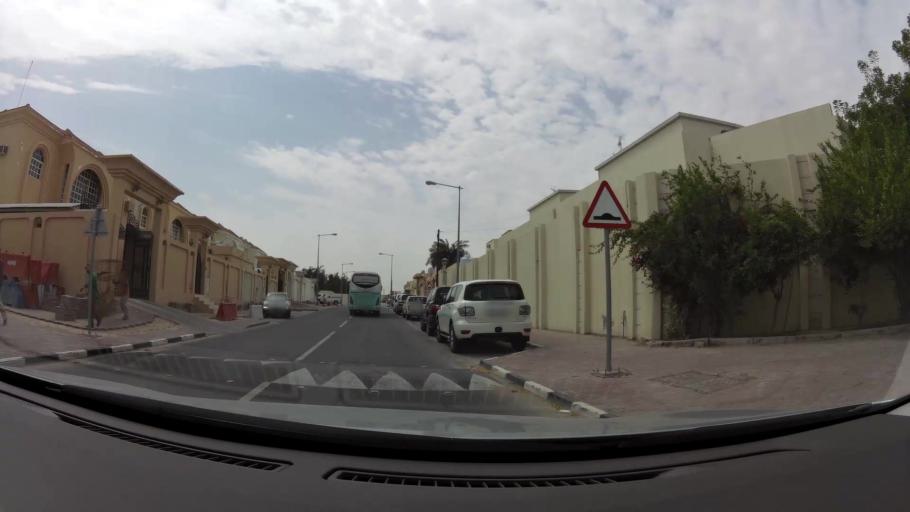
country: QA
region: Baladiyat ar Rayyan
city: Ar Rayyan
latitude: 25.3323
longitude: 51.4757
